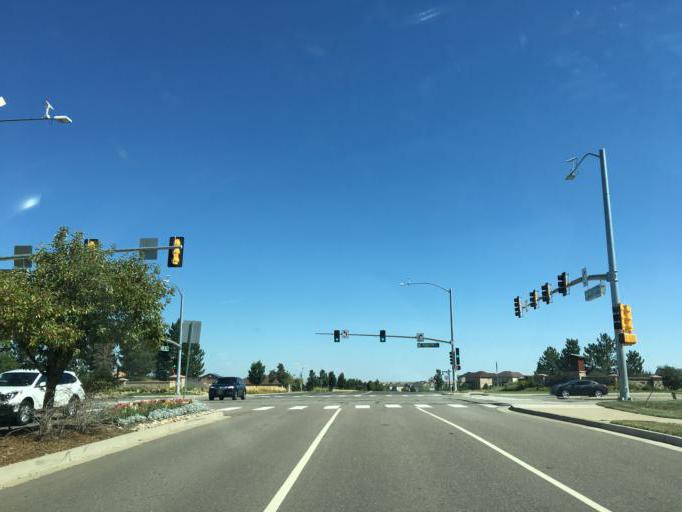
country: US
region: Colorado
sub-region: Douglas County
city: Parker
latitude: 39.5935
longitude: -104.6974
